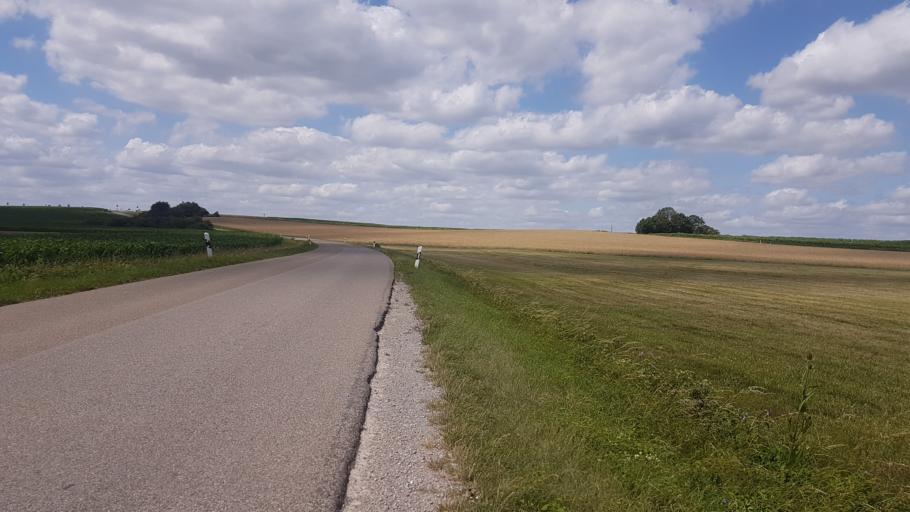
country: DE
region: Bavaria
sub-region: Regierungsbezirk Mittelfranken
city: Geslau
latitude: 49.3571
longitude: 10.3205
